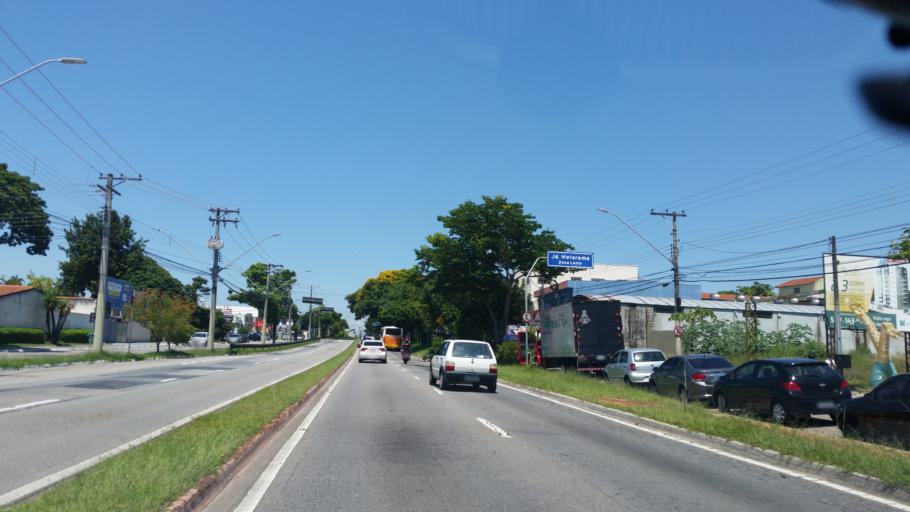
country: BR
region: Sao Paulo
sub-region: Sao Jose Dos Campos
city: Sao Jose dos Campos
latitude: -23.1753
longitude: -45.8228
